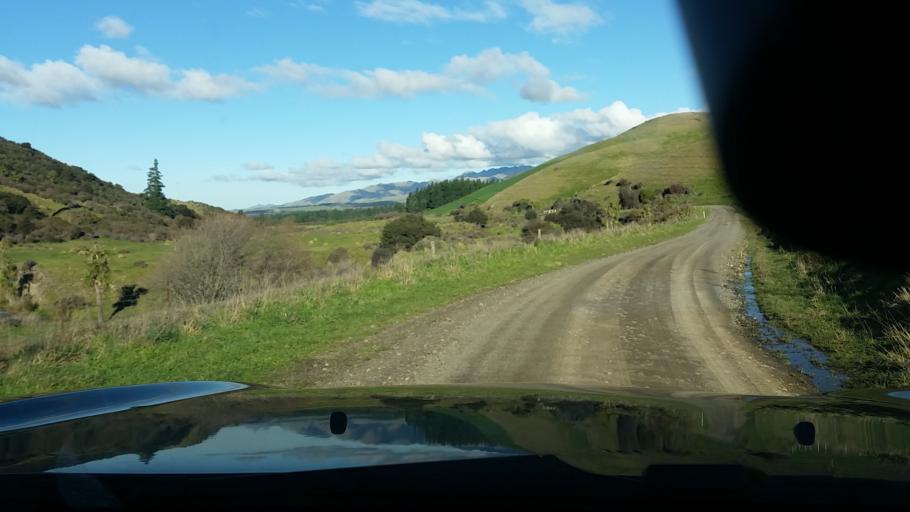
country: NZ
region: Marlborough
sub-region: Marlborough District
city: Blenheim
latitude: -41.6487
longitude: 173.9702
